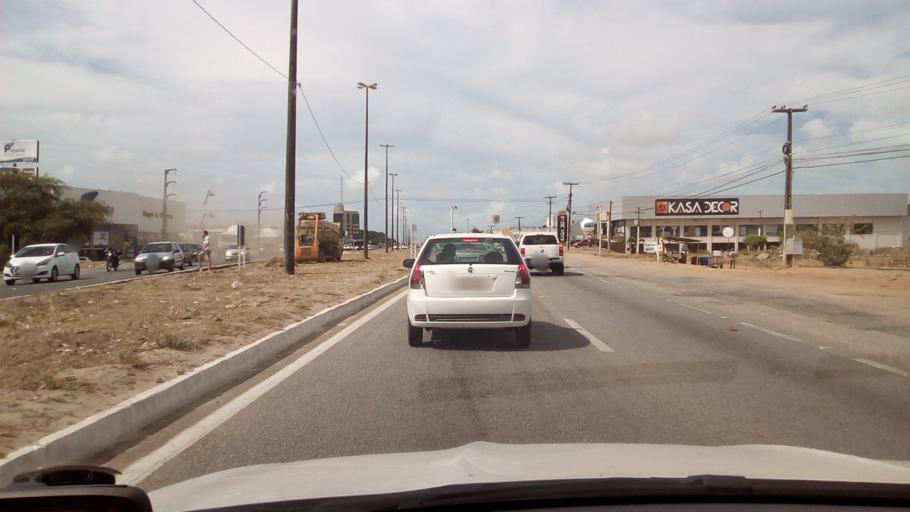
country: BR
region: Paraiba
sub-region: Joao Pessoa
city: Joao Pessoa
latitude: -7.0753
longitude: -34.8494
